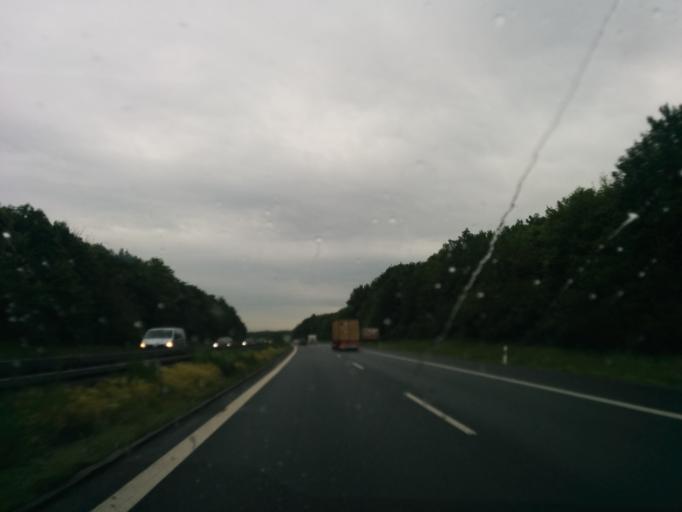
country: DE
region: Bavaria
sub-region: Regierungsbezirk Unterfranken
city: Wasserlosen
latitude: 50.0404
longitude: 10.0668
